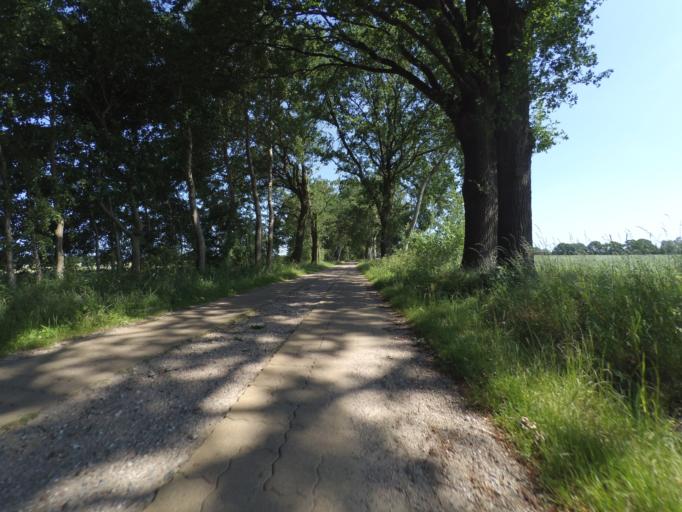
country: DE
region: Brandenburg
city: Pritzwalk
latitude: 53.1241
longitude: 12.2338
